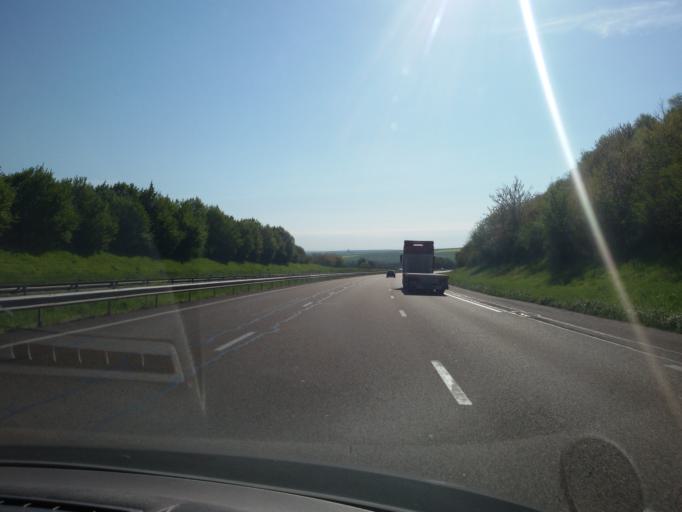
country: FR
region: Bourgogne
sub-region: Departement de l'Yonne
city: Aillant-sur-Tholon
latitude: 47.9114
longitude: 3.3235
